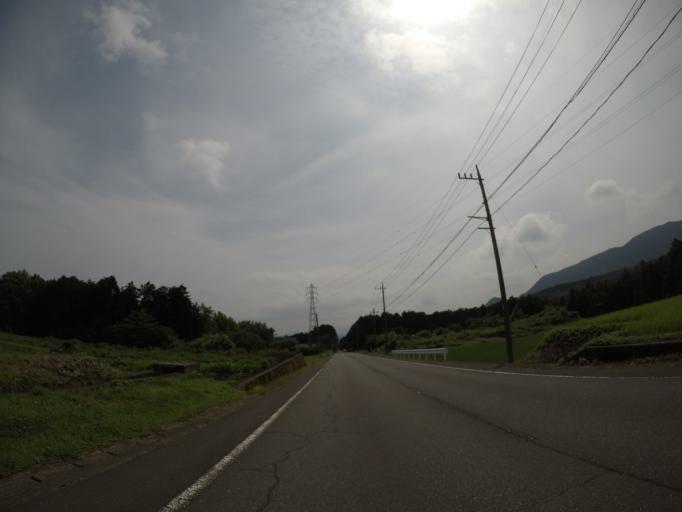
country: JP
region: Shizuoka
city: Fujinomiya
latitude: 35.2977
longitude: 138.5864
